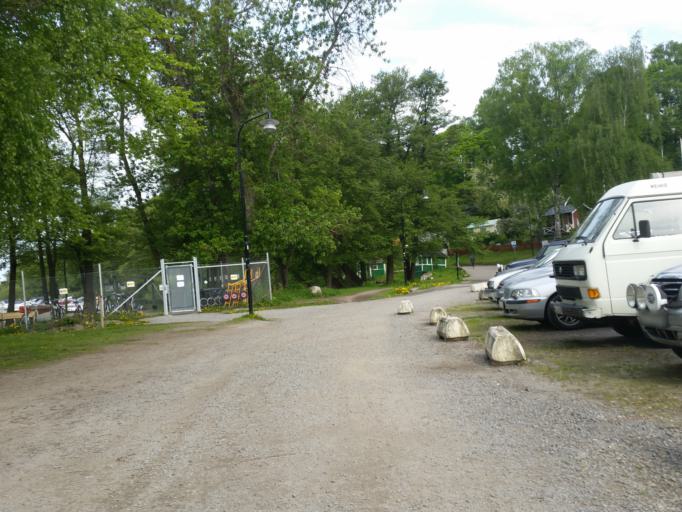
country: SE
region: Stockholm
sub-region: Stockholms Kommun
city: Arsta
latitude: 59.3042
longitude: 18.0687
